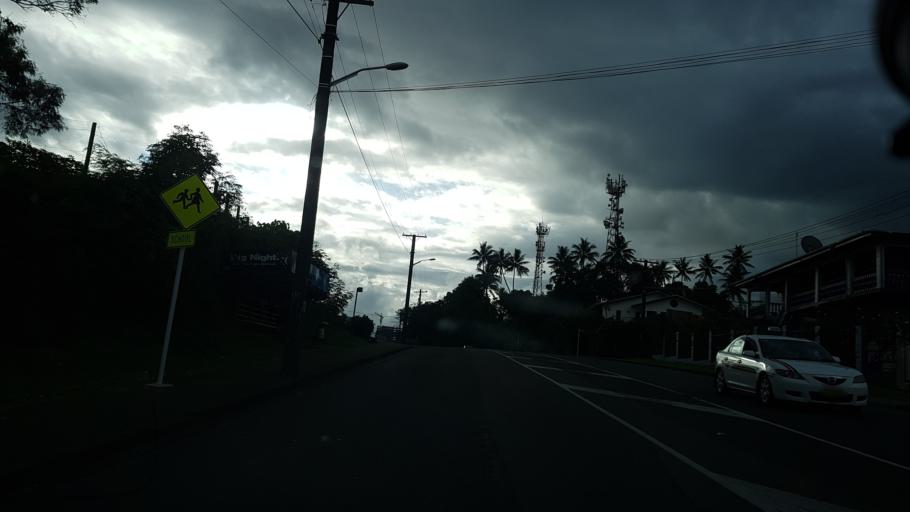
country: FJ
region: Central
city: Suva
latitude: -18.1454
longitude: 178.4420
